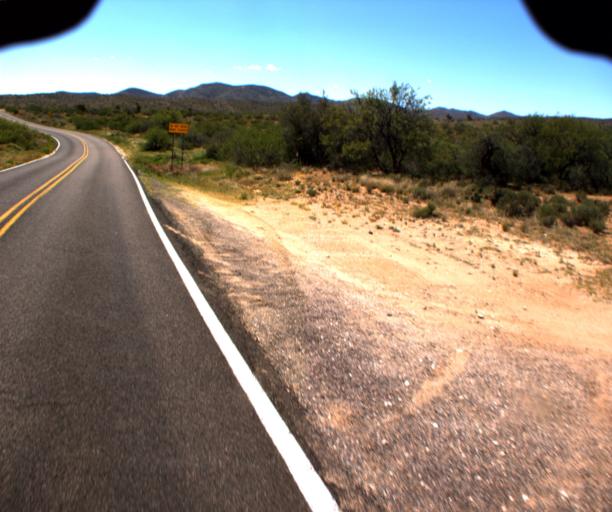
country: US
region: Arizona
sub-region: Yavapai County
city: Bagdad
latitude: 34.5182
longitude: -113.1428
